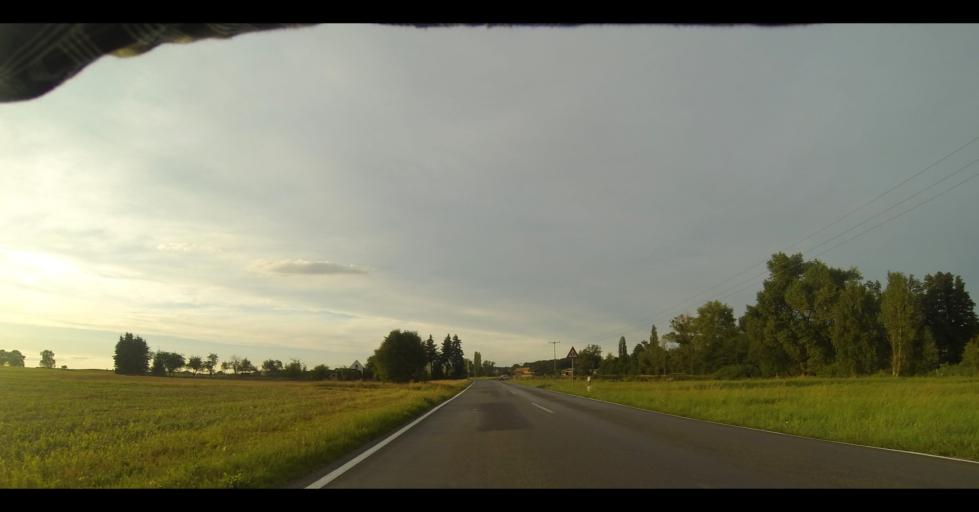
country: DE
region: Saxony
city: Moritzburg
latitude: 51.1558
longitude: 13.7326
